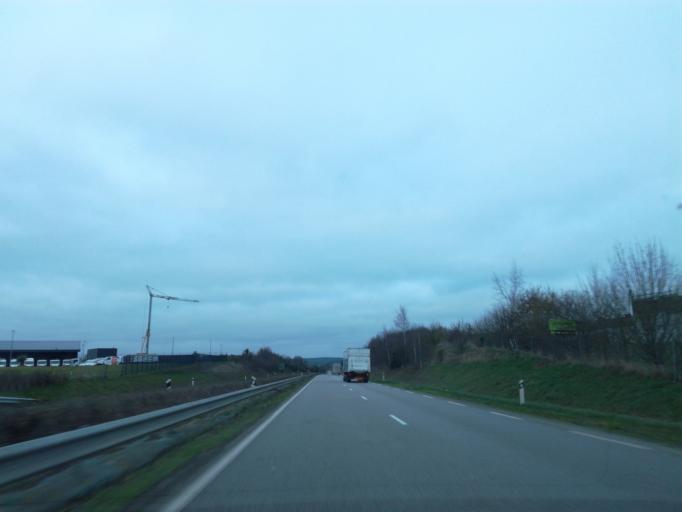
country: FR
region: Brittany
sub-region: Departement des Cotes-d'Armor
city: Loudeac
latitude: 48.1626
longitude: -2.7418
